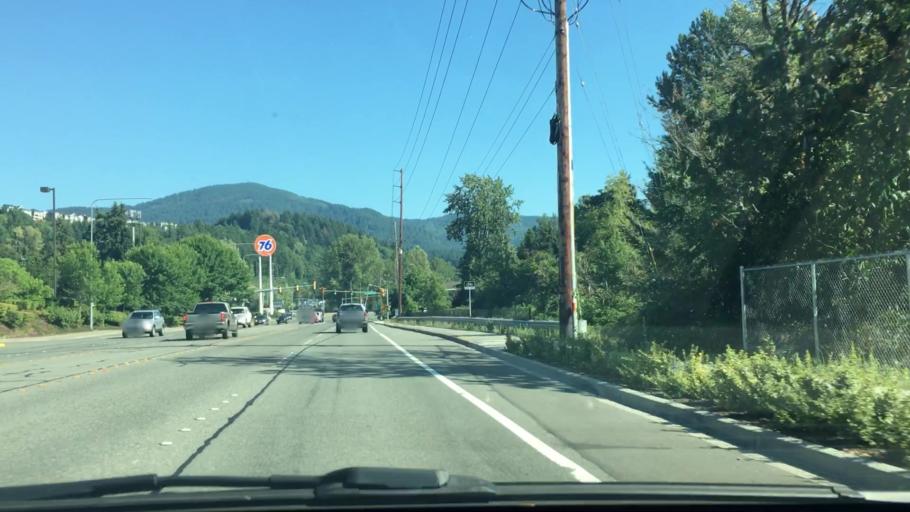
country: US
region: Washington
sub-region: King County
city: Issaquah
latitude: 47.5456
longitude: -122.0388
